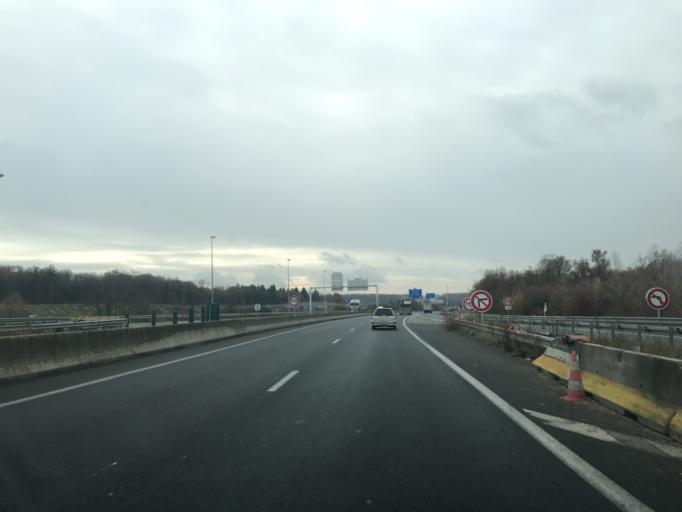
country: FR
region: Centre
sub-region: Departement d'Indre-et-Loire
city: Montbazon
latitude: 47.2979
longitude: 0.6912
